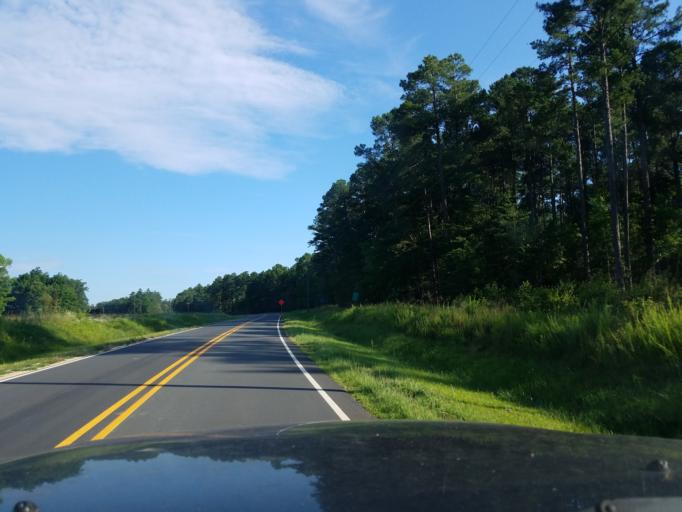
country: US
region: North Carolina
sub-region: Granville County
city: Butner
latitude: 36.1734
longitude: -78.7937
